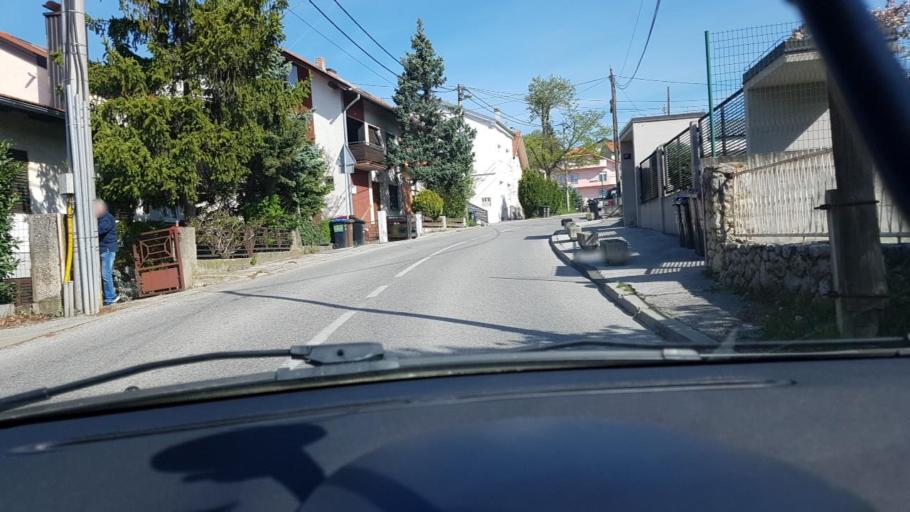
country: HR
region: Grad Zagreb
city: Zagreb
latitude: 45.8496
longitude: 15.9850
